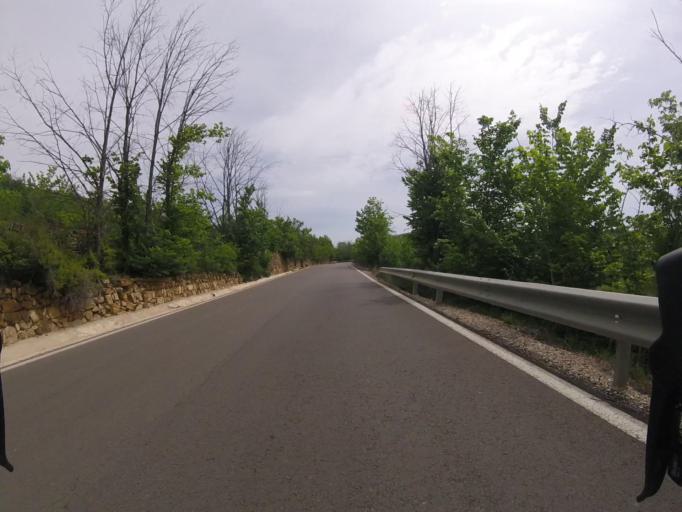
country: ES
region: Valencia
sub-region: Provincia de Castello
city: Cabanes
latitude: 40.1537
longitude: 0.0500
